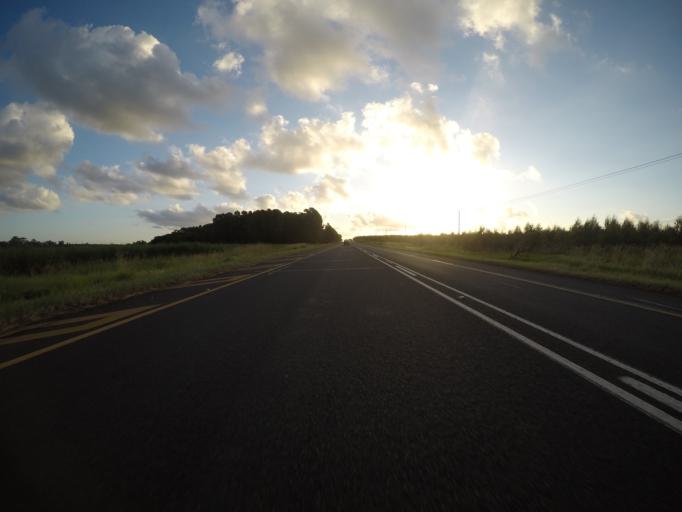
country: ZA
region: KwaZulu-Natal
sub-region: uThungulu District Municipality
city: Richards Bay
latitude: -28.6960
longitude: 31.9816
